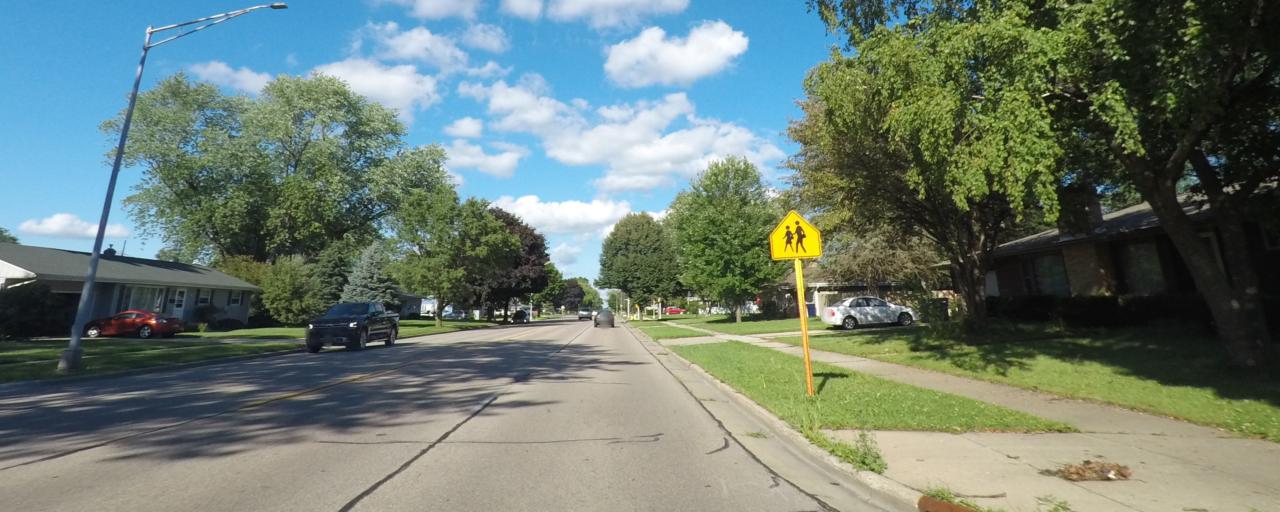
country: US
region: Wisconsin
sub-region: Rock County
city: Janesville
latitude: 42.6934
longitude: -88.9950
